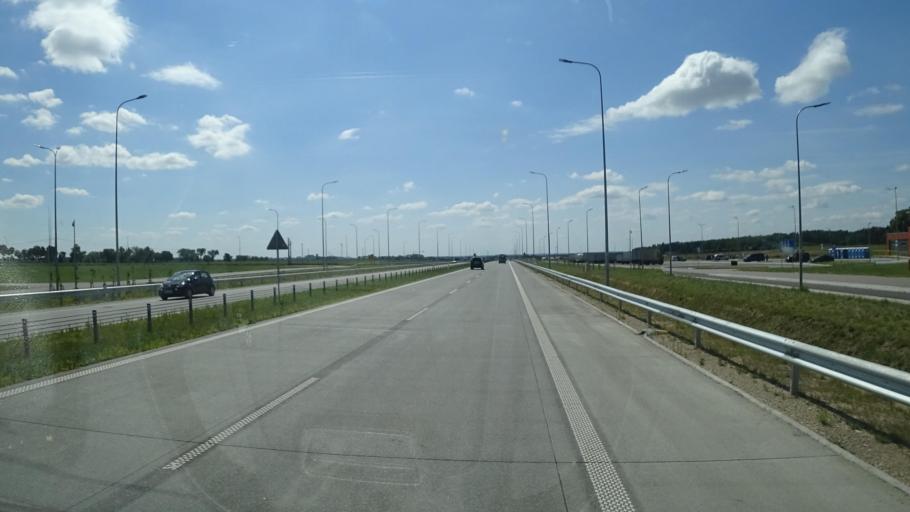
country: PL
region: Podlasie
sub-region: Powiat lomzynski
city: Piatnica
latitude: 53.2711
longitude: 22.1267
